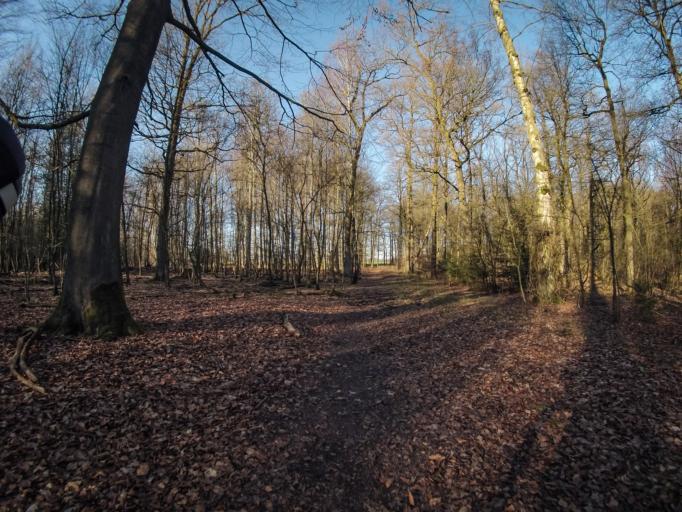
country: DE
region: Lower Saxony
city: Osnabrueck
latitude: 52.2748
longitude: 7.9867
